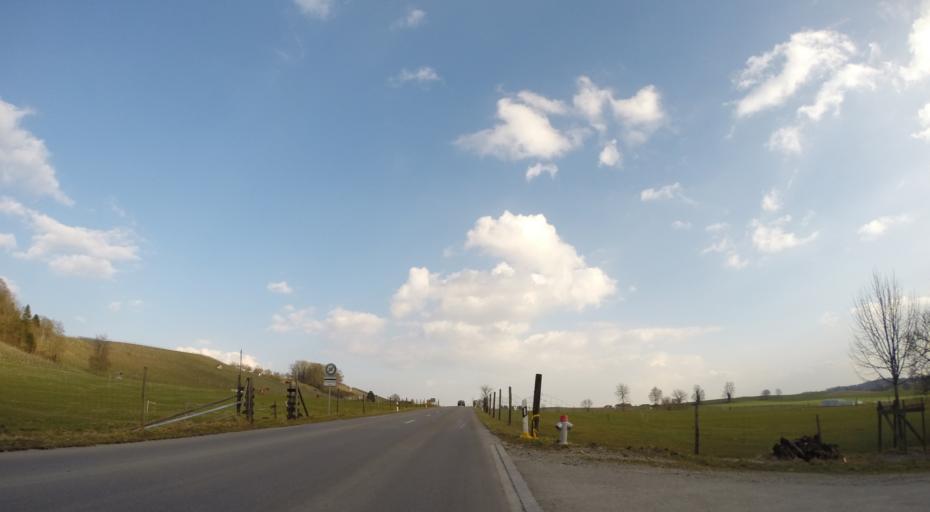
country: CH
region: Thurgau
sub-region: Frauenfeld District
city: Wagenhausen
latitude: 47.6308
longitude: 8.8033
